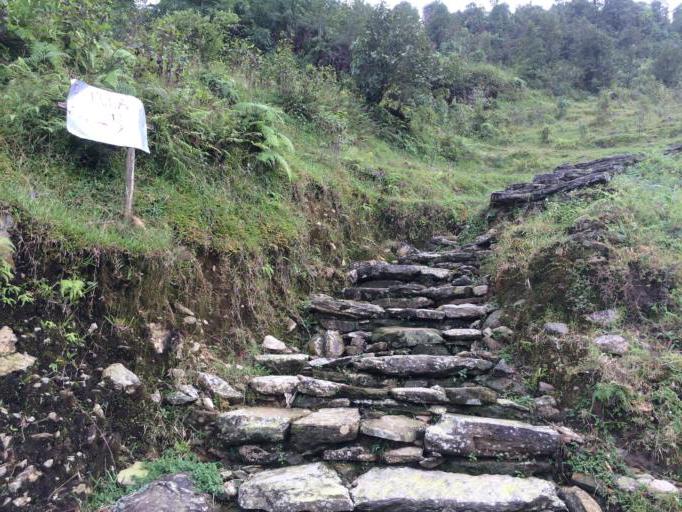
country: NP
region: Western Region
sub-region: Gandaki Zone
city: Pokhara
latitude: 28.2219
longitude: 83.8203
